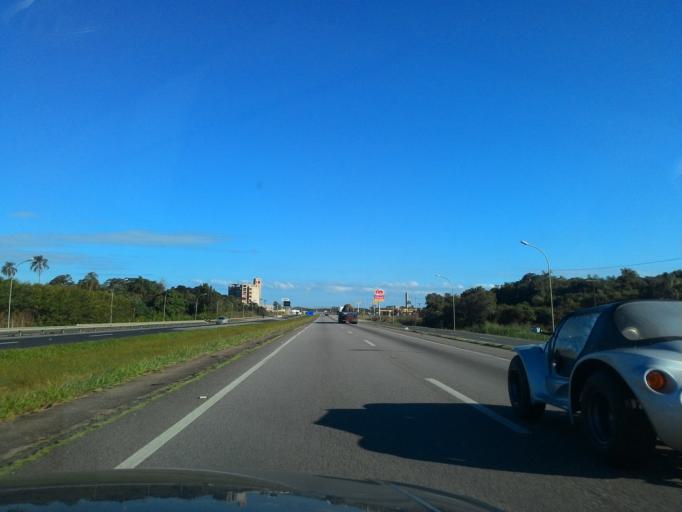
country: BR
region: Sao Paulo
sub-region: Registro
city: Registro
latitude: -24.5238
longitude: -47.8547
